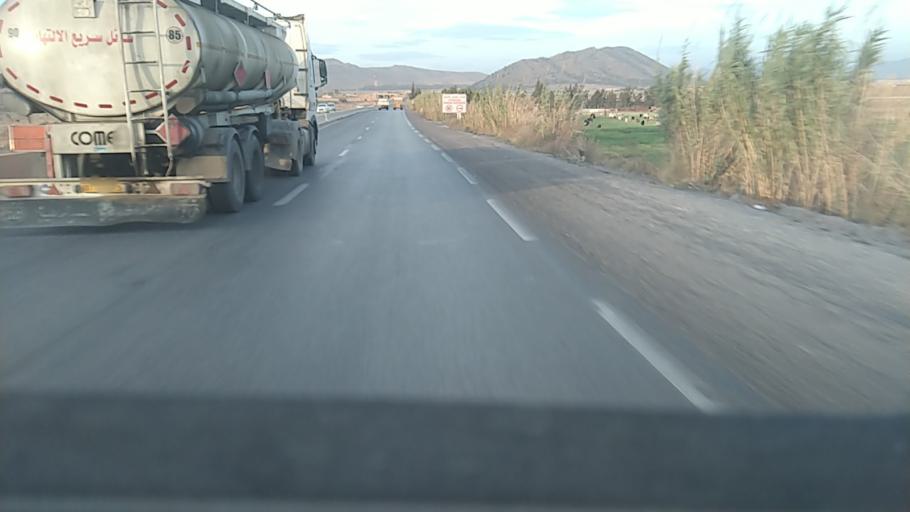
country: DZ
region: Oum el Bouaghi
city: Ain Kercha
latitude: 35.9464
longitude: 6.5234
